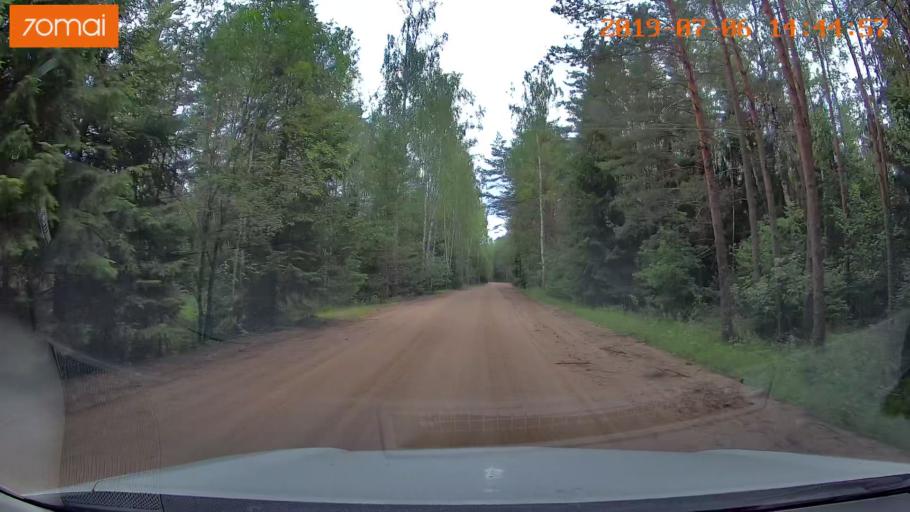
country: BY
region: Minsk
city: Ivyanyets
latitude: 53.9673
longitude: 26.6900
